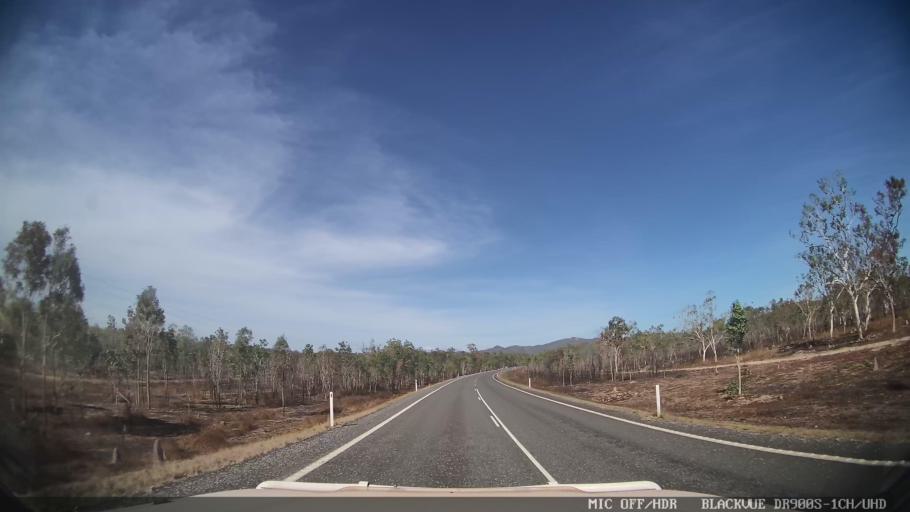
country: AU
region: Queensland
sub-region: Cook
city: Cooktown
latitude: -15.6964
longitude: 145.0413
